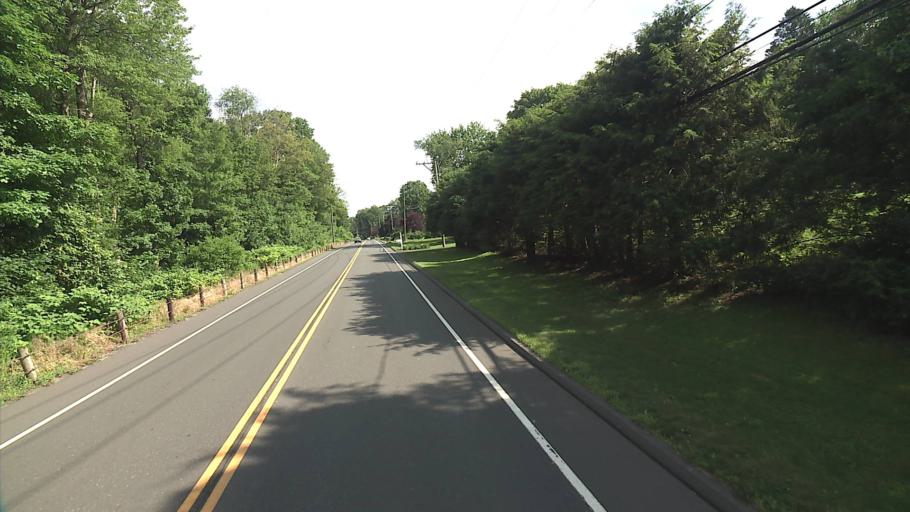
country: US
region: Connecticut
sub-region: New Haven County
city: Waterbury
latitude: 41.5493
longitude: -73.0914
